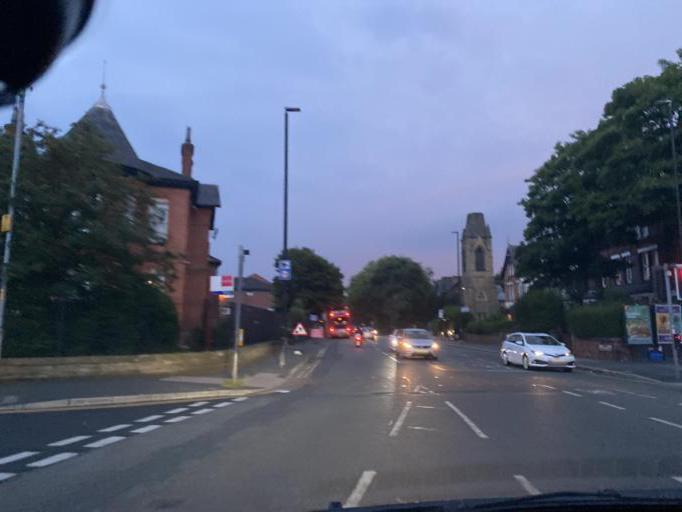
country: GB
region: England
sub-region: Manchester
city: Hulme
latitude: 53.4588
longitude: -2.2583
